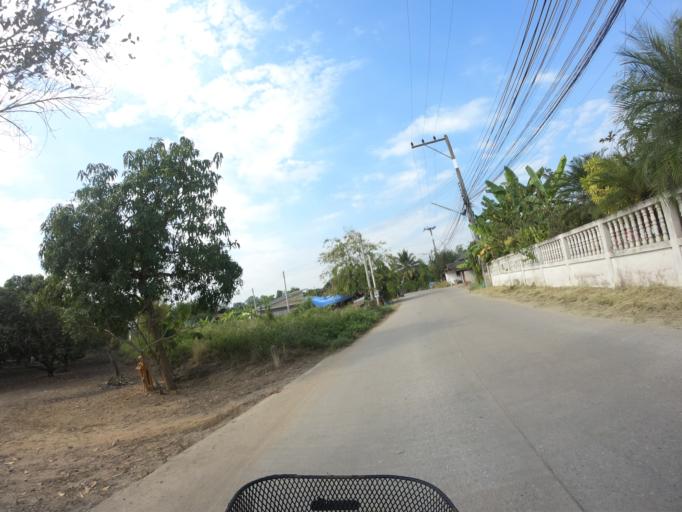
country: TH
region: Chiang Mai
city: Saraphi
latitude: 18.7226
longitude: 99.0598
